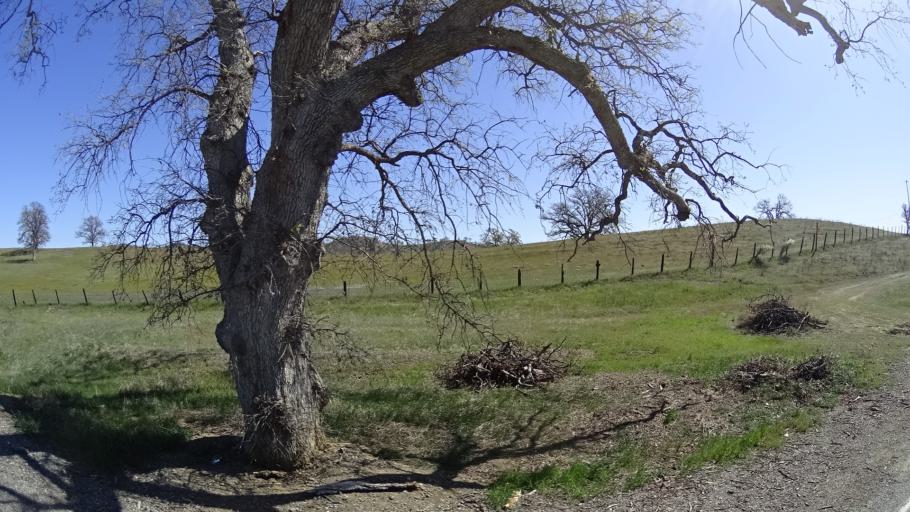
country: US
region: California
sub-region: Glenn County
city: Orland
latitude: 39.6846
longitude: -122.5388
